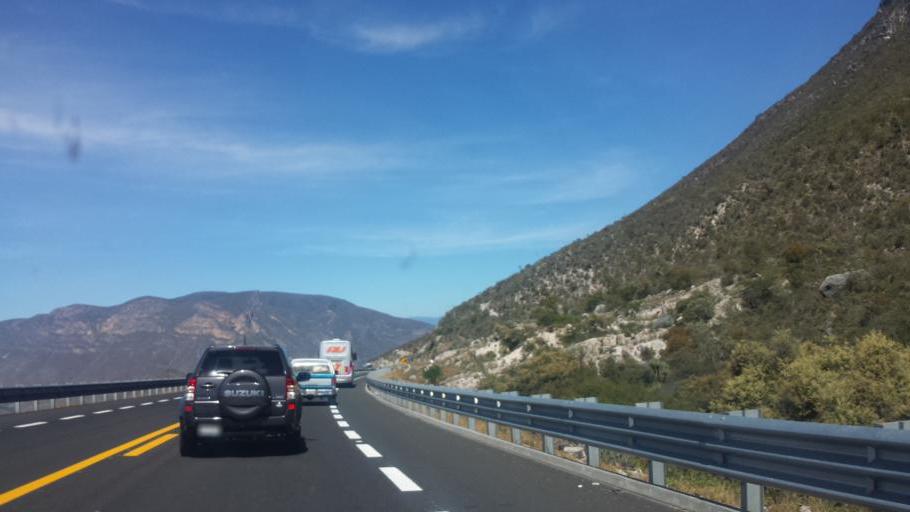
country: MX
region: Puebla
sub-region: San Jose Miahuatlan
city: San Pedro Tetitlan
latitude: 18.0759
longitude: -97.3524
